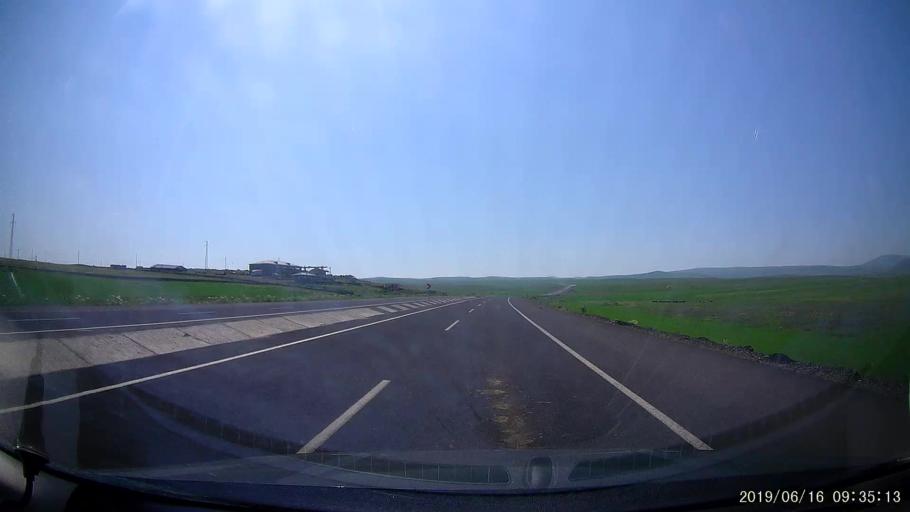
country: TR
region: Kars
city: Kars
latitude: 40.5751
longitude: 43.1520
